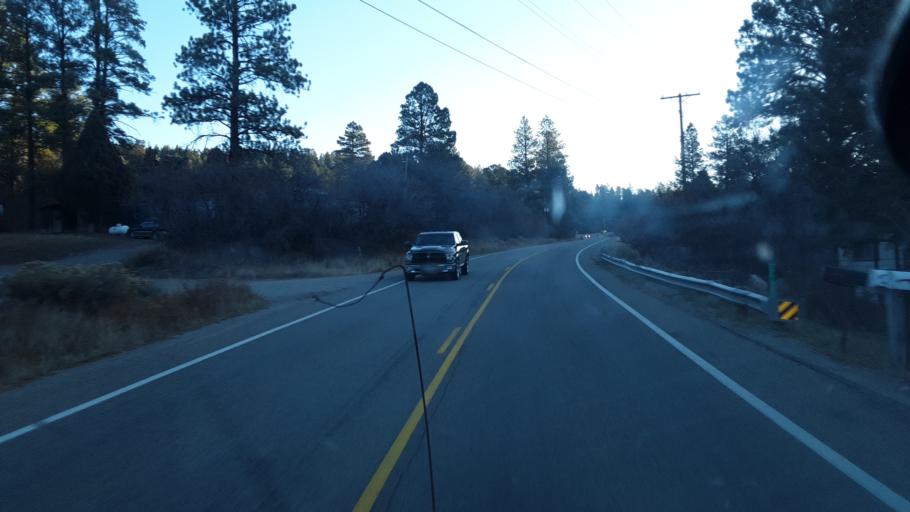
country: US
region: Colorado
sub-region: La Plata County
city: Durango
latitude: 37.3122
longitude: -107.8066
